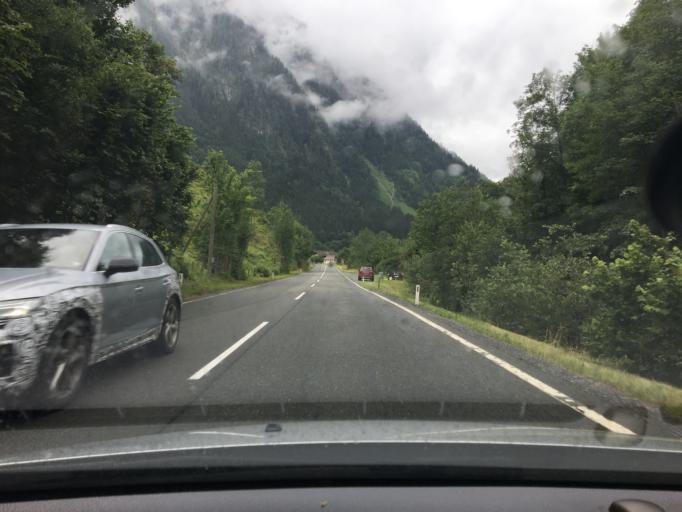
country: AT
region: Salzburg
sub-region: Politischer Bezirk Zell am See
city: Bruck an der Grossglocknerstrasse
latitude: 47.2051
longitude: 12.8327
